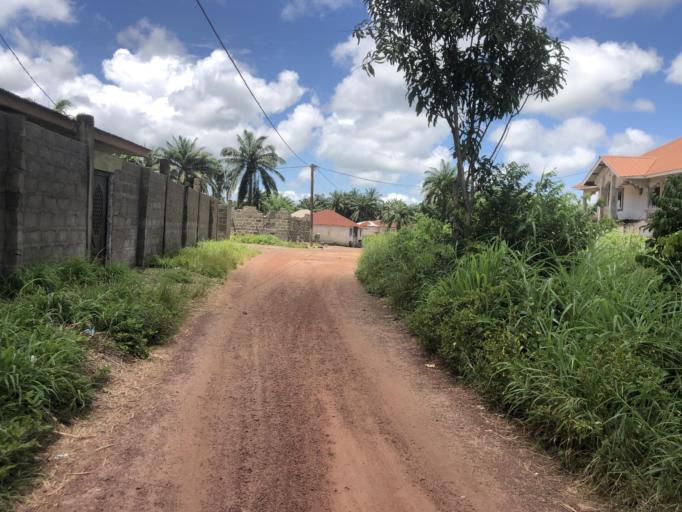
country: SL
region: Northern Province
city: Makeni
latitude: 8.8616
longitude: -12.0471
